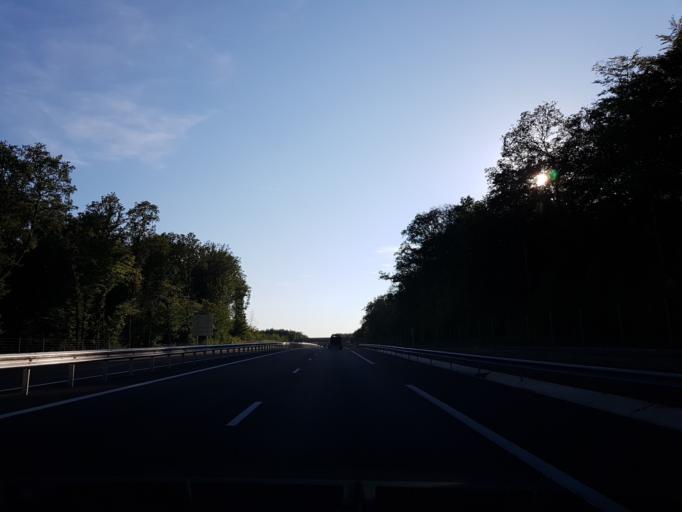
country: FR
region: Franche-Comte
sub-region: Departement de la Haute-Saone
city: Magny-Vernois
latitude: 47.6926
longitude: 6.4544
